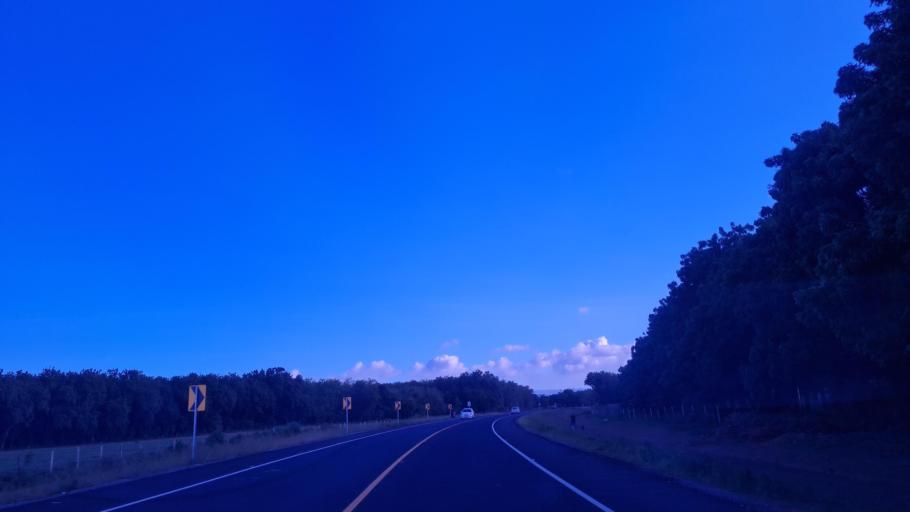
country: NI
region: Masaya
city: Ticuantepe
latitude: 12.0967
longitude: -86.1596
